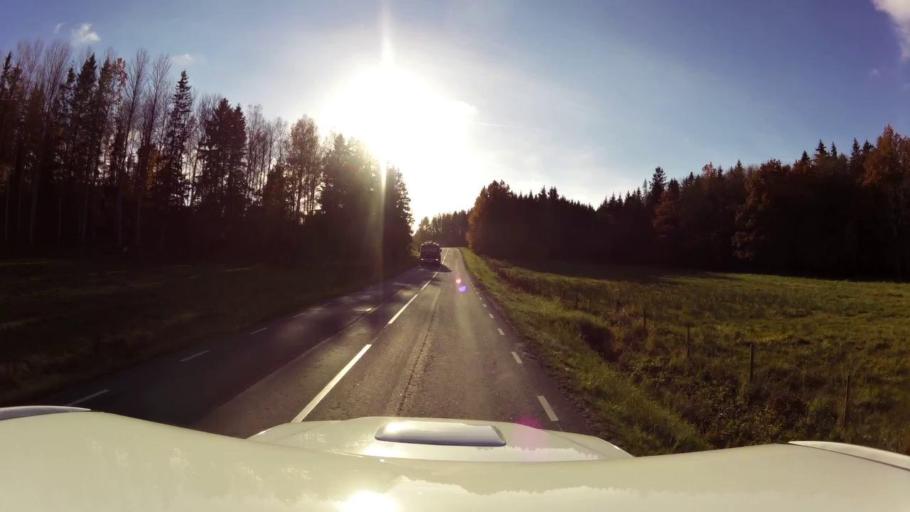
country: SE
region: OEstergoetland
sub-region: Linkopings Kommun
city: Malmslatt
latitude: 58.3239
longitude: 15.5025
